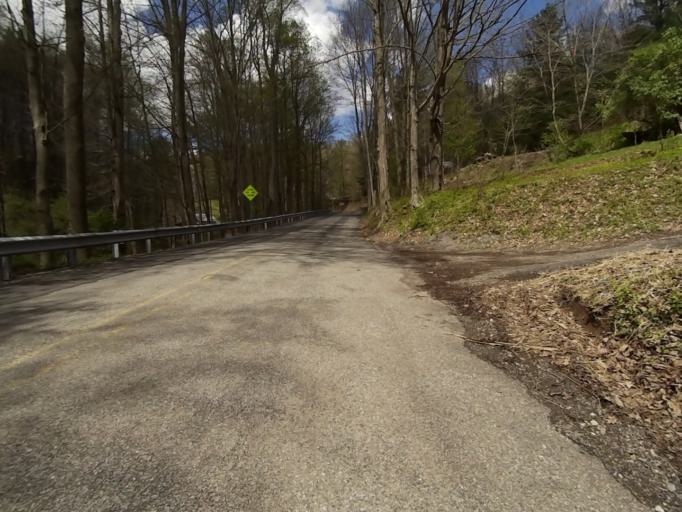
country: US
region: Pennsylvania
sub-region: Centre County
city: Milesburg
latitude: 40.9570
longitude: -77.8909
